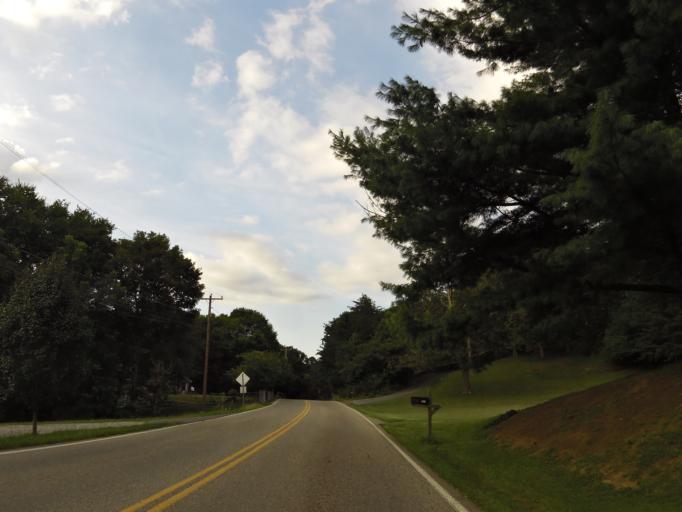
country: US
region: Tennessee
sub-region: Jefferson County
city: Dandridge
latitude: 35.9255
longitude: -83.3404
